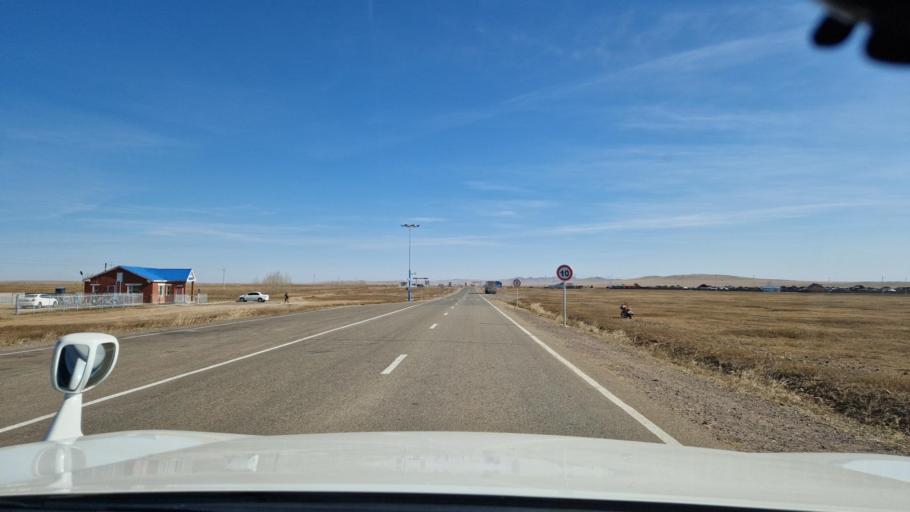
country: MN
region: Suhbaatar
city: Hanhohiy
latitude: 47.5797
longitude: 112.3443
